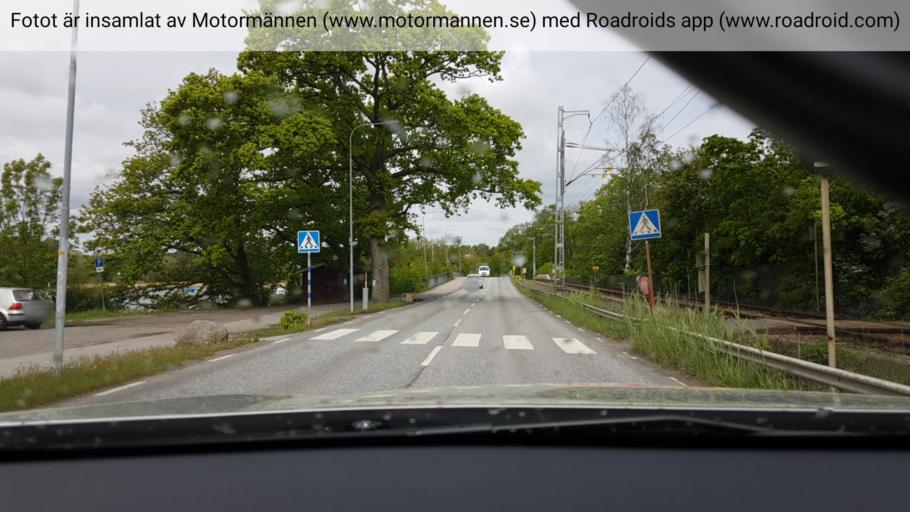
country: SE
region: Stockholm
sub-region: Nacka Kommun
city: Saltsjobaden
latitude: 59.2851
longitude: 18.2969
